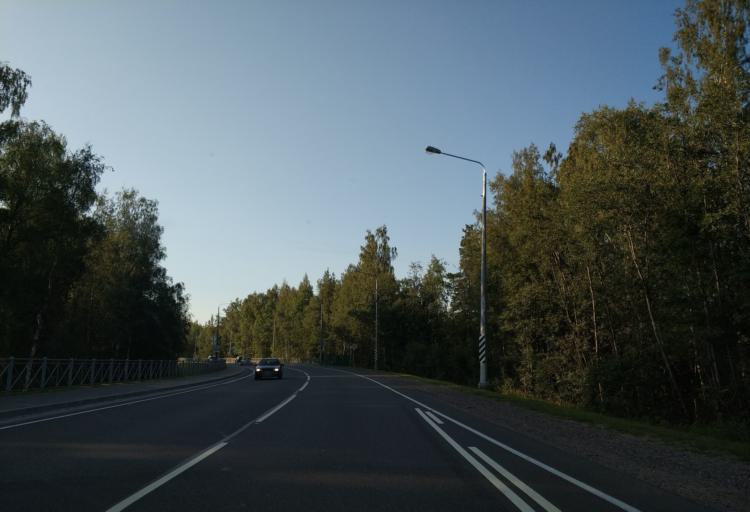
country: RU
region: Leningrad
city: Sapernoye
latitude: 60.7005
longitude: 29.9724
